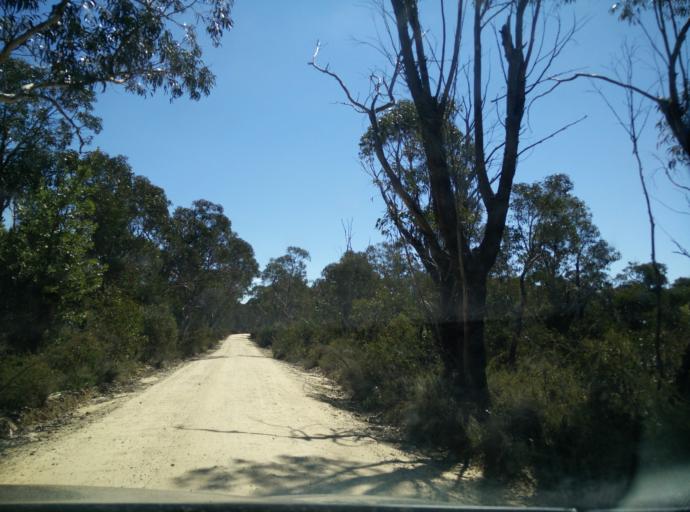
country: AU
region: New South Wales
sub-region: Blue Mountains Municipality
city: Blackheath
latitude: -33.5818
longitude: 150.2747
